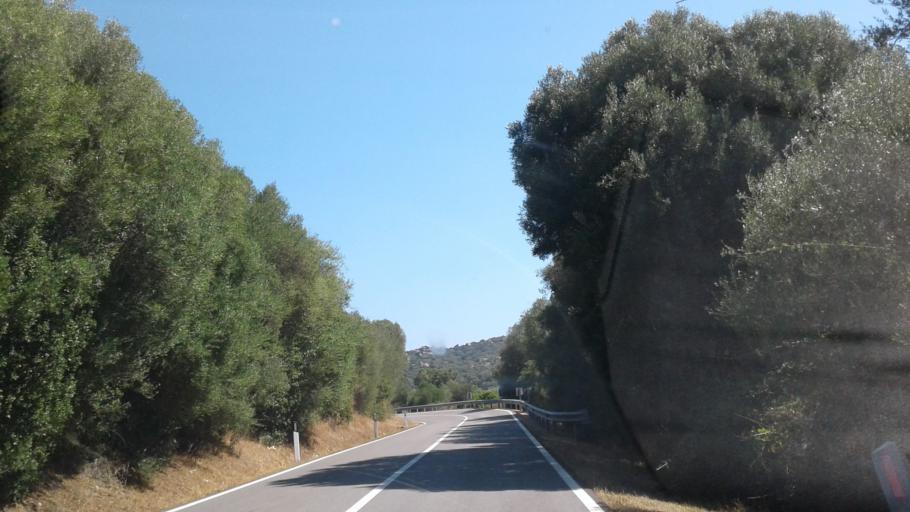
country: IT
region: Sardinia
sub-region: Provincia di Olbia-Tempio
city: Palau
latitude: 41.1497
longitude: 9.3137
